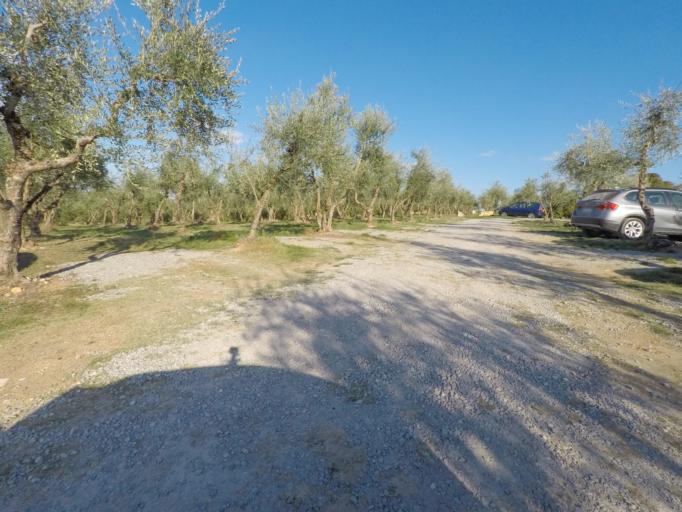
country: IT
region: Tuscany
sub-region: Provincia di Siena
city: Radda in Chianti
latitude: 43.4416
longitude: 11.3904
